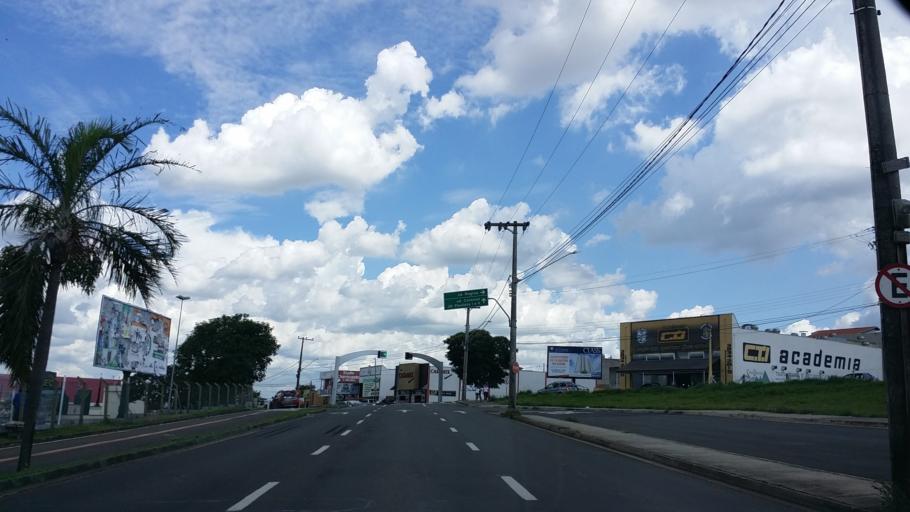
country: BR
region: Sao Paulo
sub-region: Indaiatuba
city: Indaiatuba
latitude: -23.0964
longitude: -47.2292
